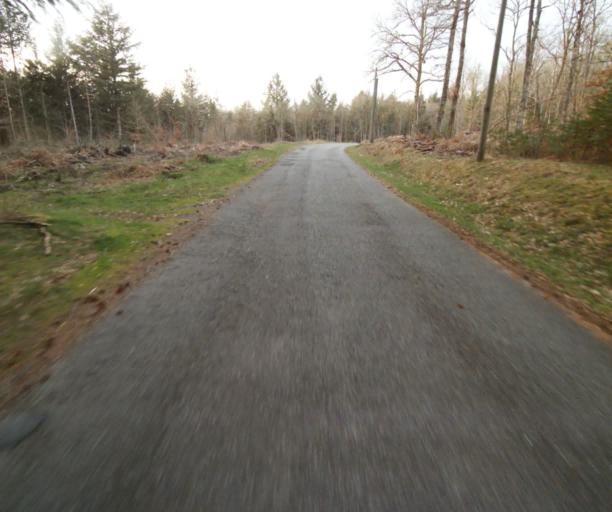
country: FR
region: Limousin
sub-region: Departement de la Correze
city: Argentat
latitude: 45.2488
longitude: 1.9763
